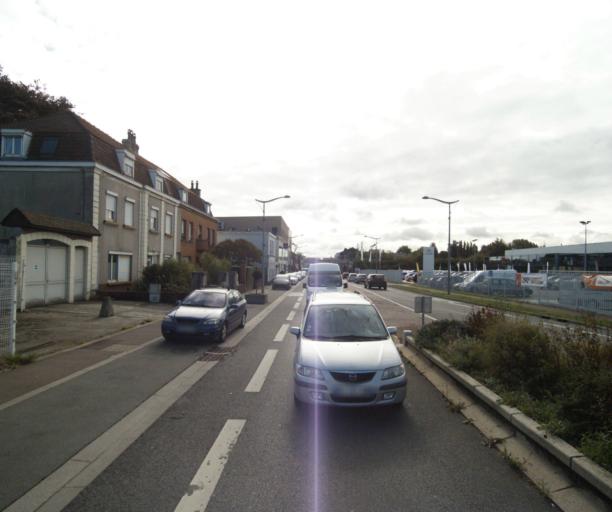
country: FR
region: Nord-Pas-de-Calais
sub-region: Departement du Nord
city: Lambersart
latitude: 50.6457
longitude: 3.0111
